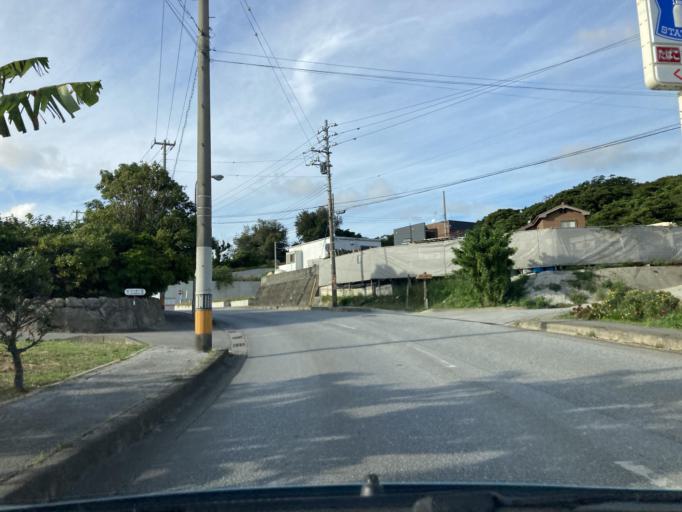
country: JP
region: Okinawa
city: Tomigusuku
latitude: 26.1460
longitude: 127.7451
